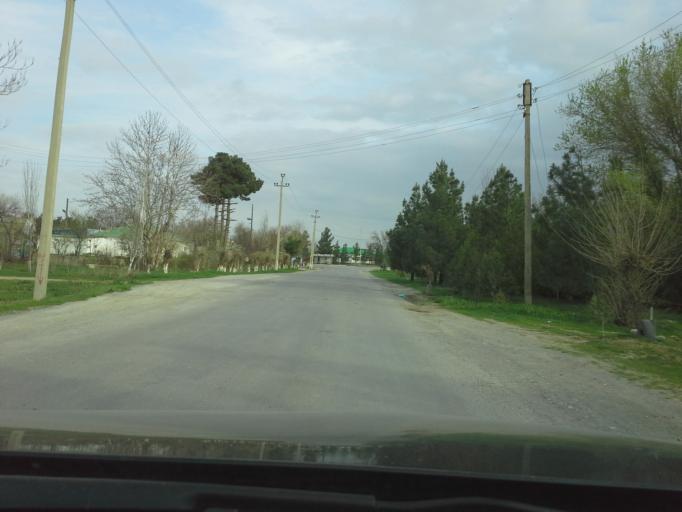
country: TM
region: Ahal
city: Abadan
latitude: 37.9353
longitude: 58.2254
